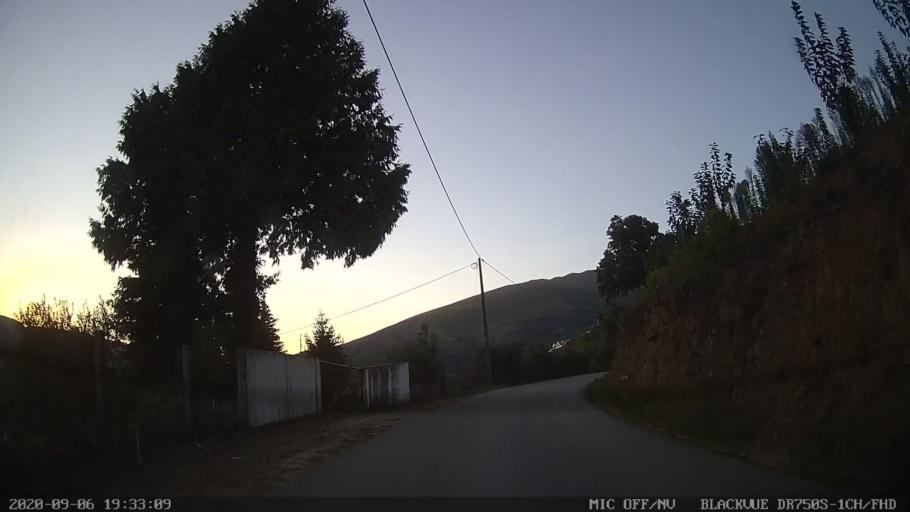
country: PT
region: Vila Real
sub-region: Mesao Frio
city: Mesao Frio
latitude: 41.1767
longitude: -7.9008
